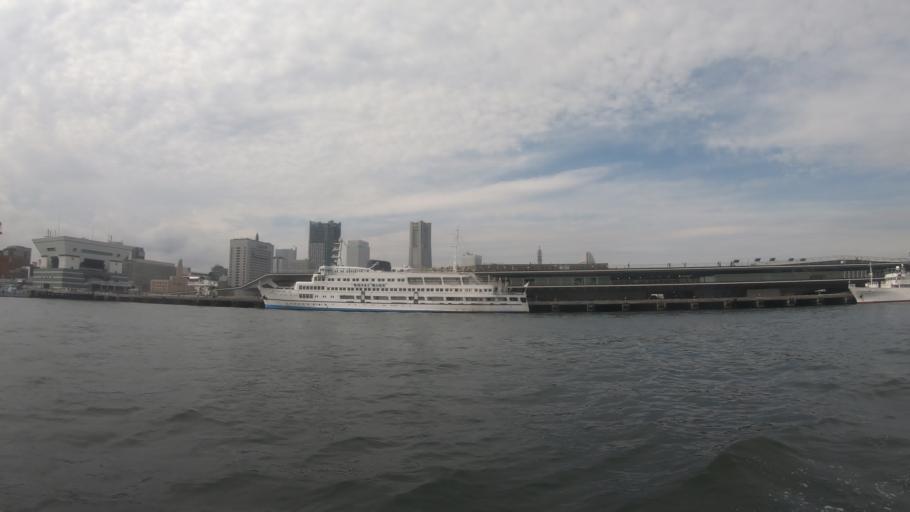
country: JP
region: Kanagawa
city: Yokohama
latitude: 35.4505
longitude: 139.6492
